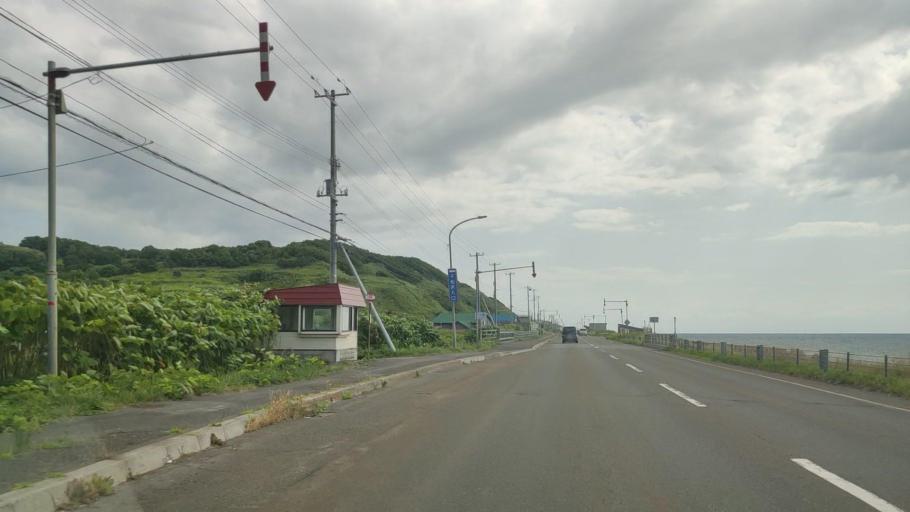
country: JP
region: Hokkaido
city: Rumoi
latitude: 44.1820
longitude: 141.6588
